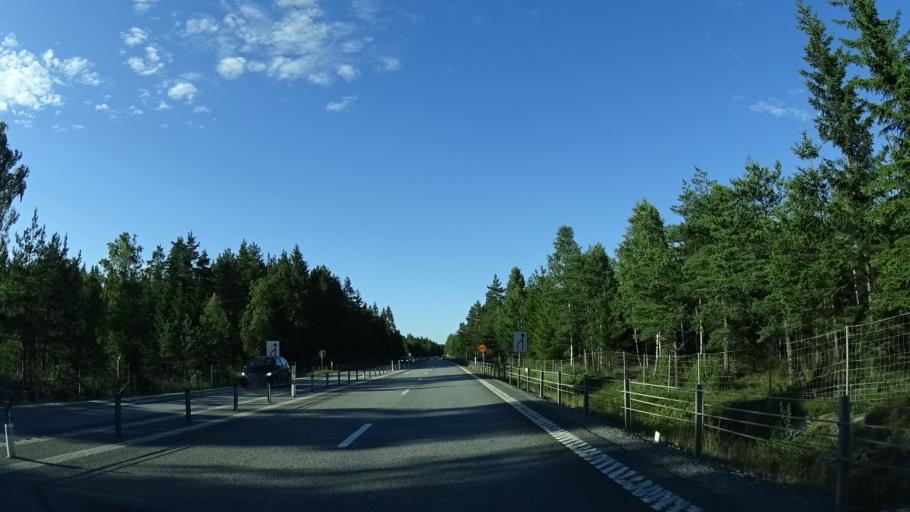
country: SE
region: Stockholm
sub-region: Osterakers Kommun
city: Akersberga
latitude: 59.6018
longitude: 18.2755
